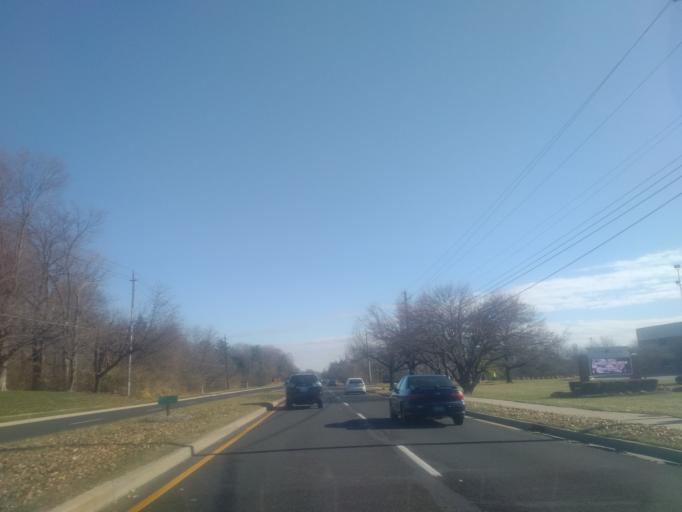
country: US
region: Indiana
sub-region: Marion County
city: Meridian Hills
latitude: 39.9125
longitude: -86.1293
